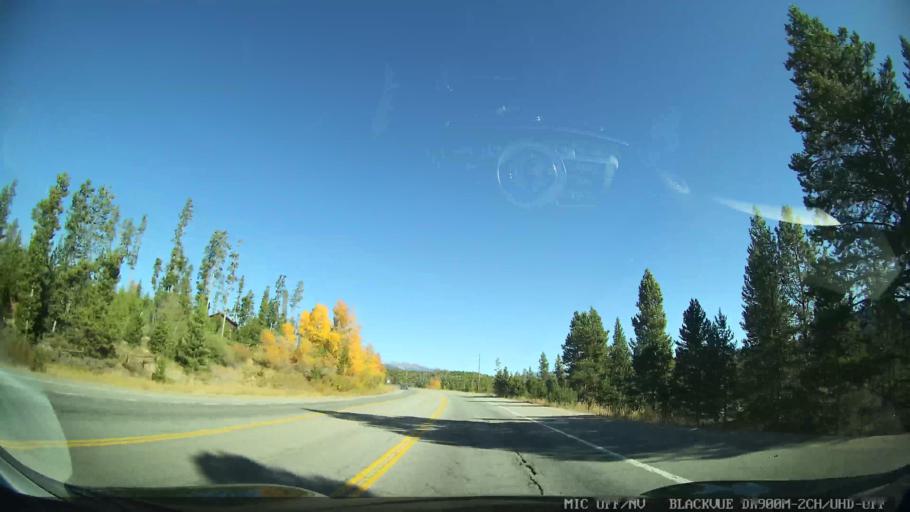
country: US
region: Colorado
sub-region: Grand County
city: Granby
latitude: 40.2071
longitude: -105.8603
